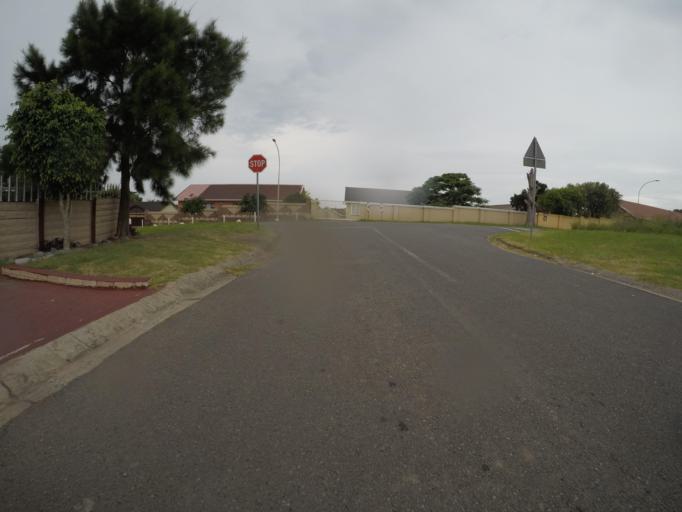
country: ZA
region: Eastern Cape
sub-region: Buffalo City Metropolitan Municipality
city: East London
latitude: -32.9998
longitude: 27.8505
